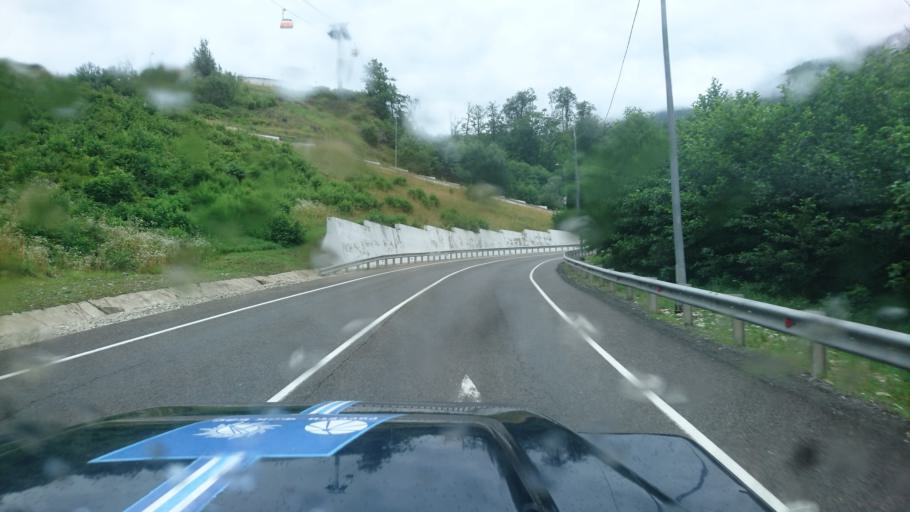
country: RU
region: Krasnodarskiy
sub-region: Sochi City
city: Krasnaya Polyana
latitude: 43.6729
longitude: 40.2859
